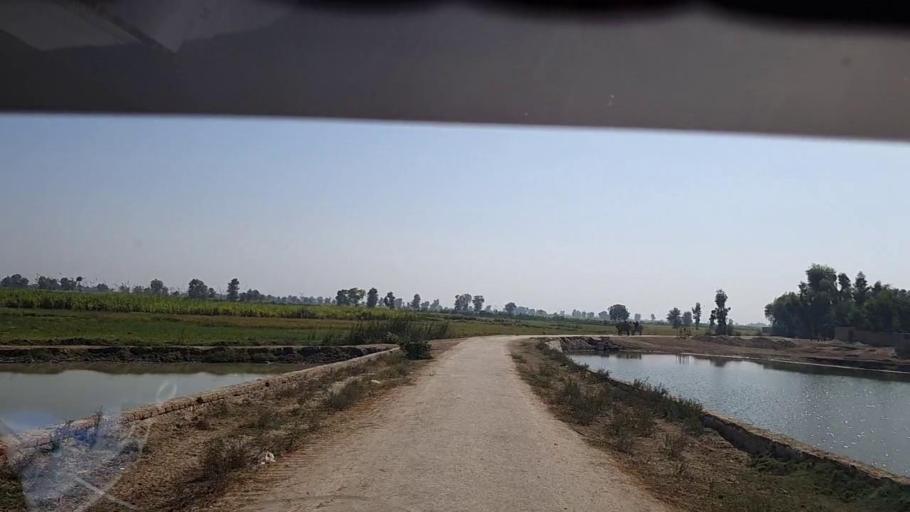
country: PK
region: Sindh
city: Naudero
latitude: 27.6997
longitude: 68.4056
